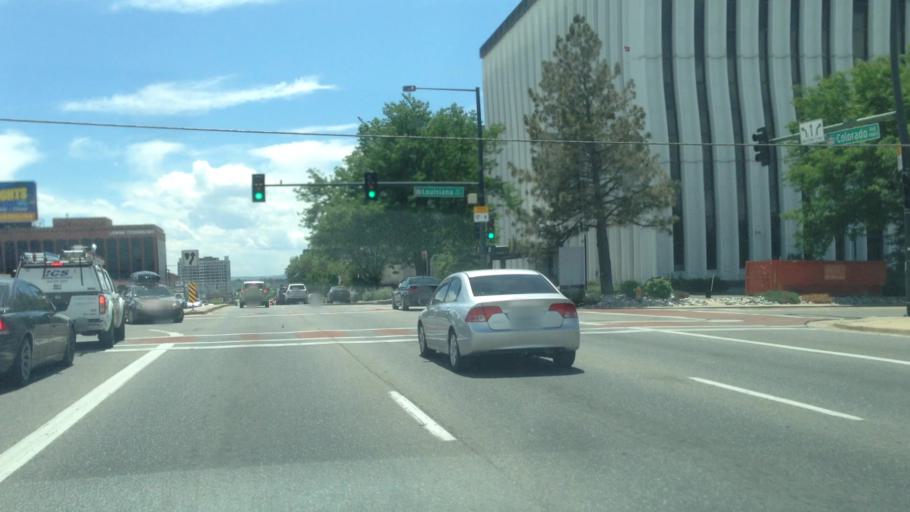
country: US
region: Colorado
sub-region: Arapahoe County
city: Glendale
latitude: 39.6932
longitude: -104.9407
